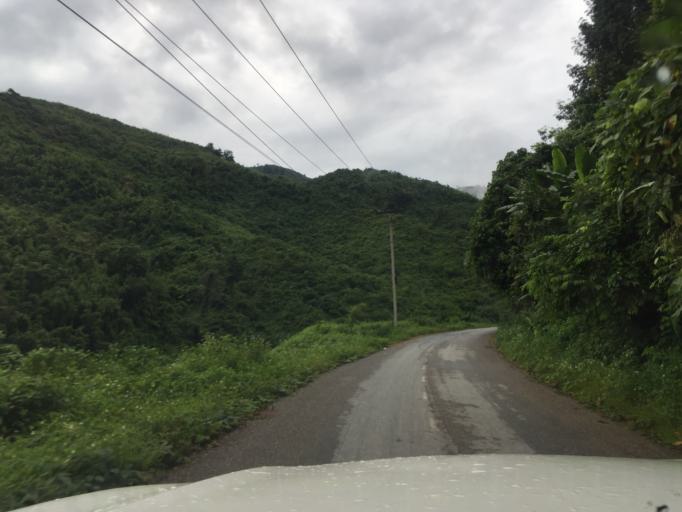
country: LA
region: Oudomxai
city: Muang La
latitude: 21.0142
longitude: 102.2324
